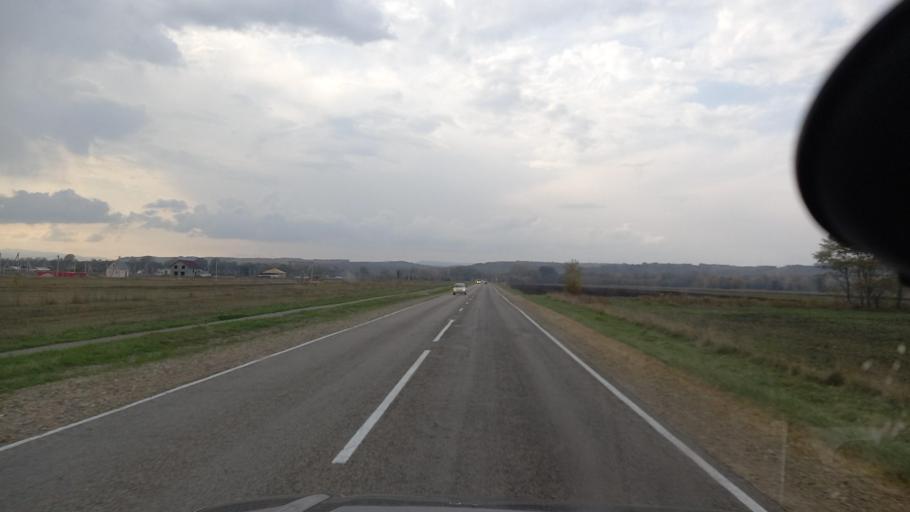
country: RU
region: Krasnodarskiy
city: Mostovskoy
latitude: 44.3922
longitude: 40.7629
